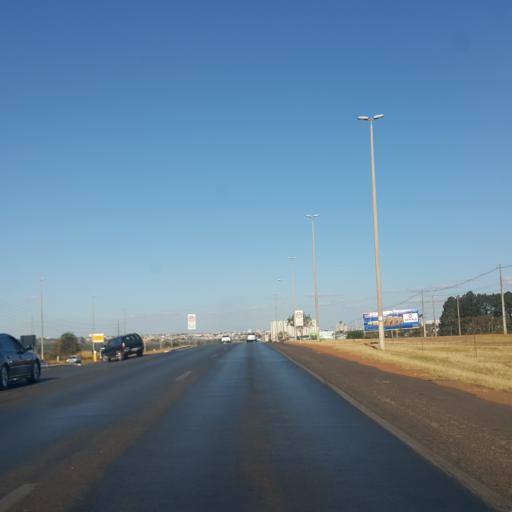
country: BR
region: Federal District
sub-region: Brasilia
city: Brasilia
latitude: -15.7877
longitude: -48.1148
